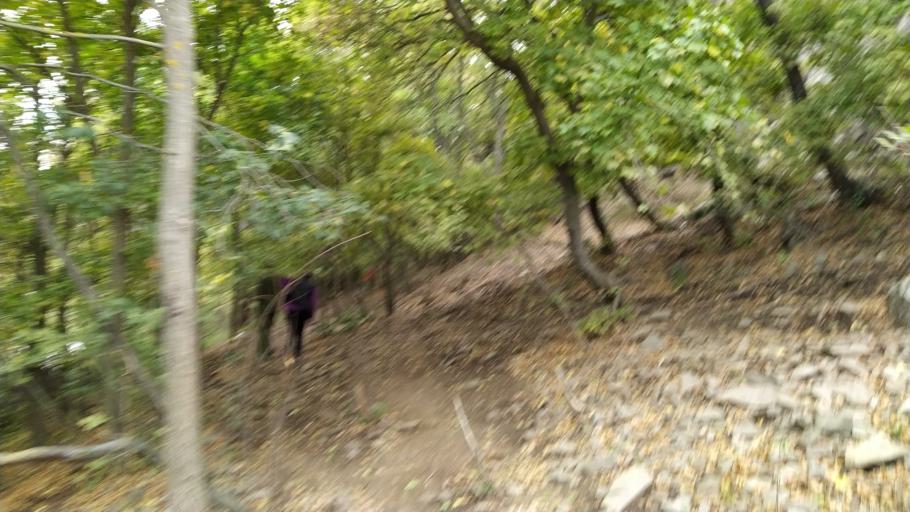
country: RU
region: Rostov
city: Gornyy
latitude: 47.8910
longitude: 40.2469
